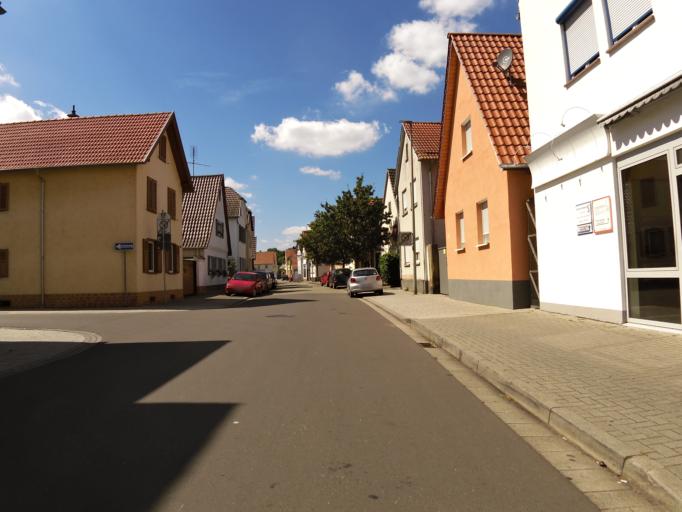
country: DE
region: Rheinland-Pfalz
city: Bellheim
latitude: 49.1918
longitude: 8.2842
